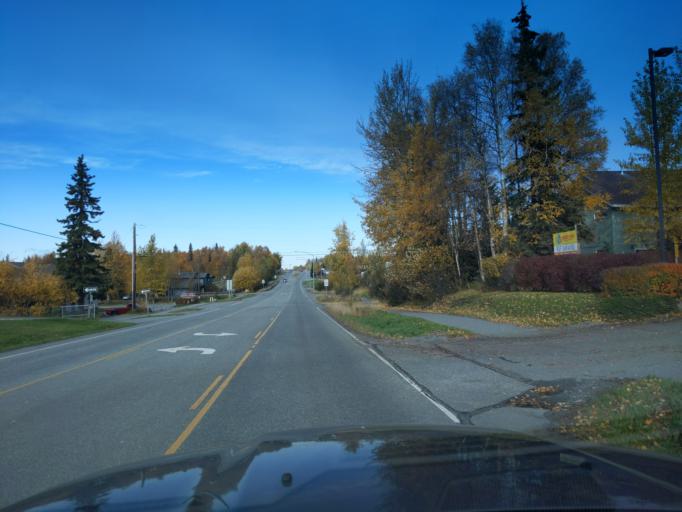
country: US
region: Alaska
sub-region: Anchorage Municipality
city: Anchorage
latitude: 61.1532
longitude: -149.9519
